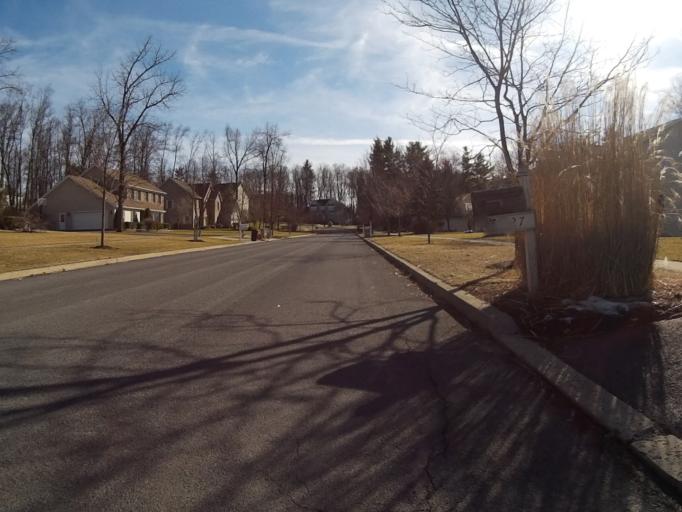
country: US
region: Pennsylvania
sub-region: Centre County
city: State College
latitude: 40.7935
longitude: -77.8893
